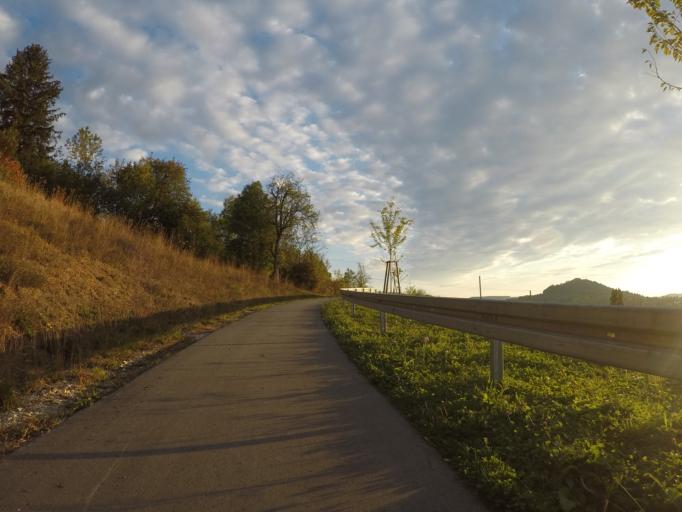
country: DE
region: Baden-Wuerttemberg
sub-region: Tuebingen Region
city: Pfullingen
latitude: 48.4849
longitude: 9.2343
